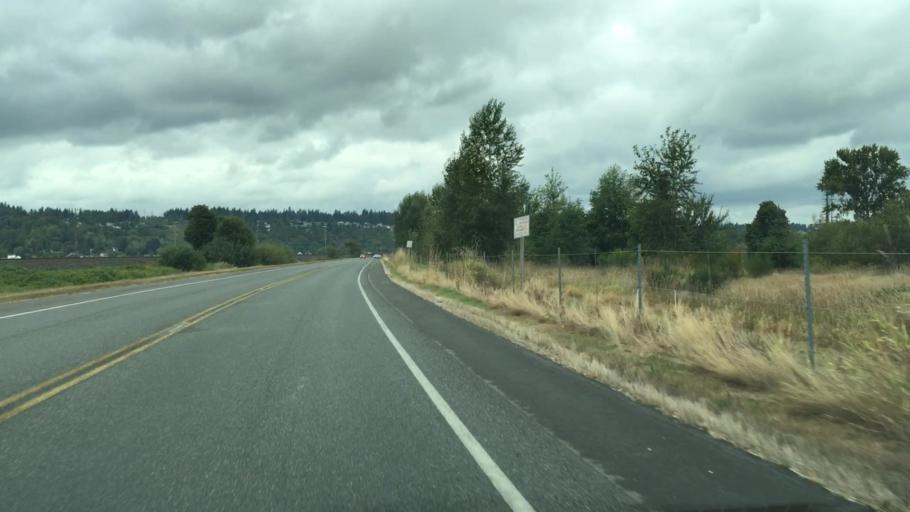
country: US
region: Washington
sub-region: Snohomish County
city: Fobes Hill
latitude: 47.9249
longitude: -122.1637
